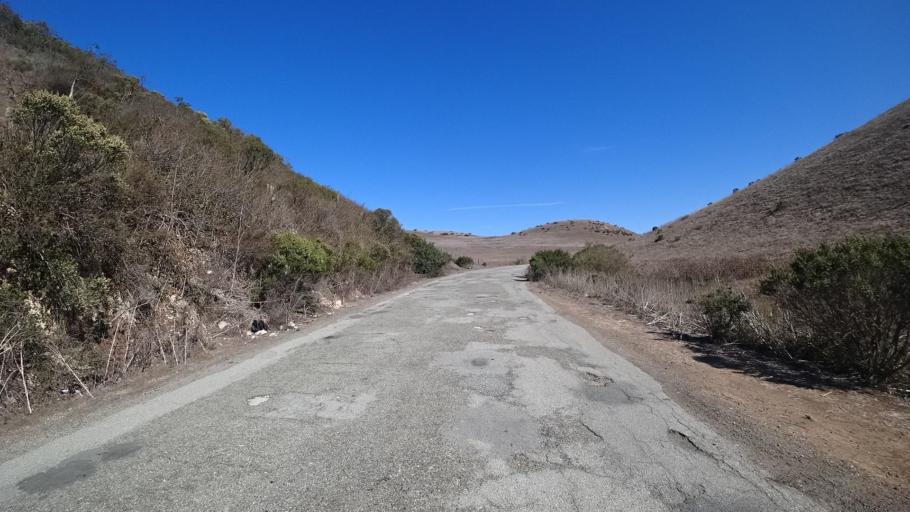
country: US
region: California
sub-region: San Benito County
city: San Juan Bautista
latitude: 36.8191
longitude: -121.5734
